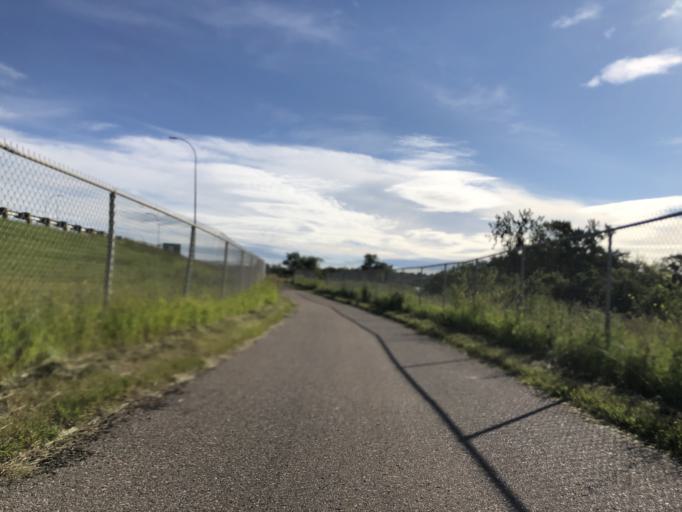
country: CA
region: Alberta
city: Calgary
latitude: 50.9808
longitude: -114.0363
